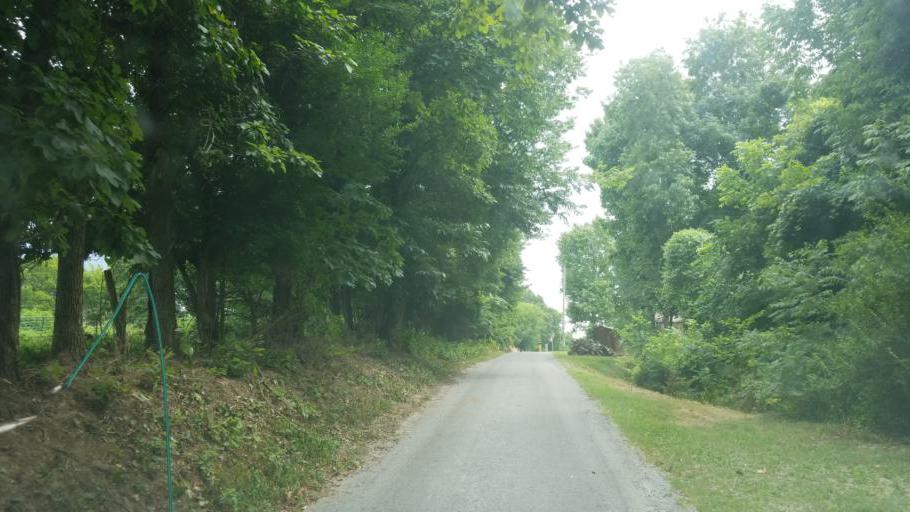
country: US
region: Illinois
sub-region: Jackson County
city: Murphysboro
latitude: 37.7043
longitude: -89.3478
